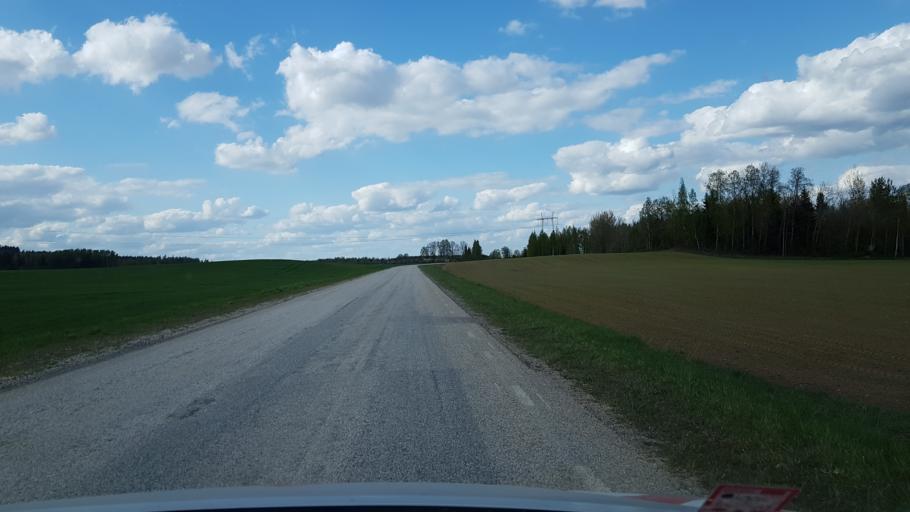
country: EE
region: Tartu
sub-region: UElenurme vald
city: Ulenurme
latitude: 58.2711
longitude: 26.9084
